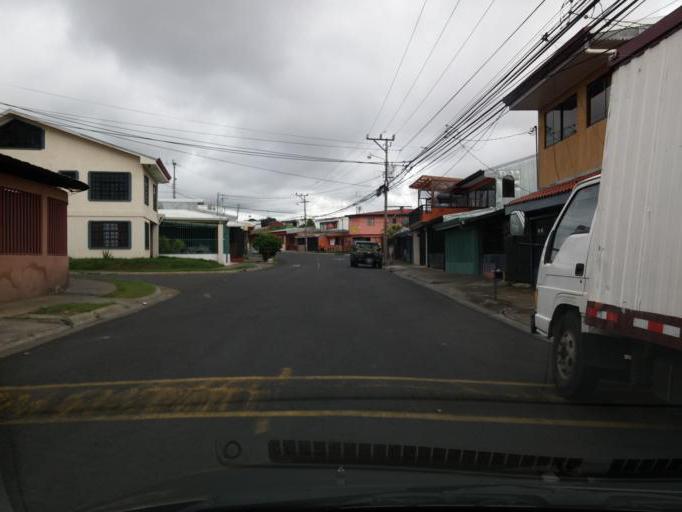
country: CR
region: Heredia
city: Mercedes
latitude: 10.0230
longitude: -84.1293
